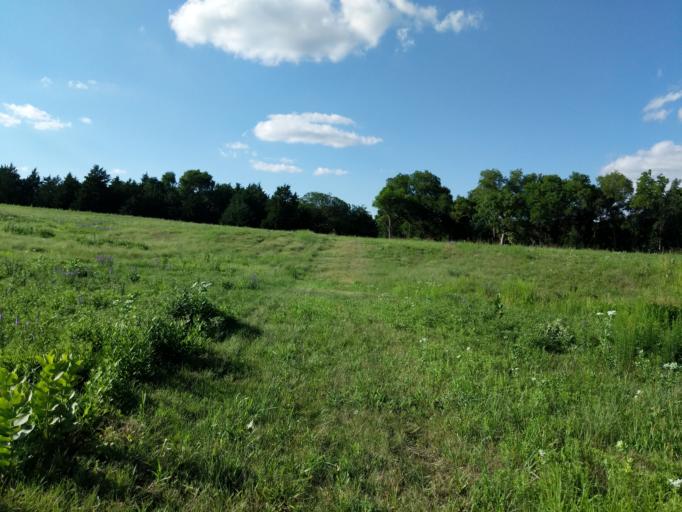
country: US
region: Kansas
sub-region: Smith County
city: Smith Center
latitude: 39.8880
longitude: -98.9484
